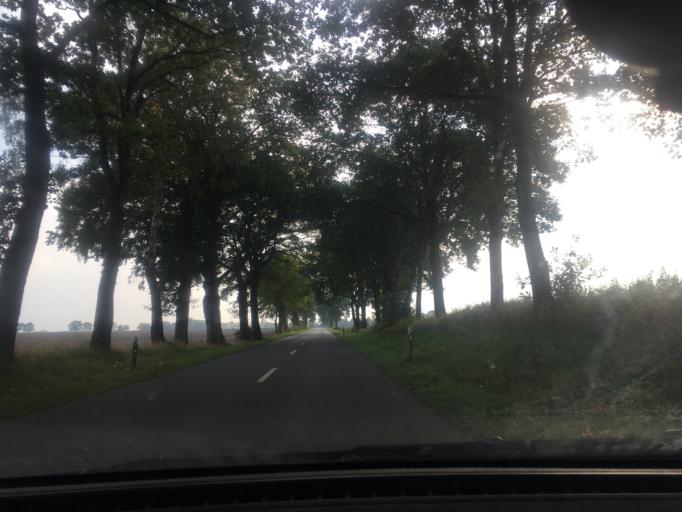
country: DE
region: Lower Saxony
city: Vastorf
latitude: 53.2125
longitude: 10.5518
